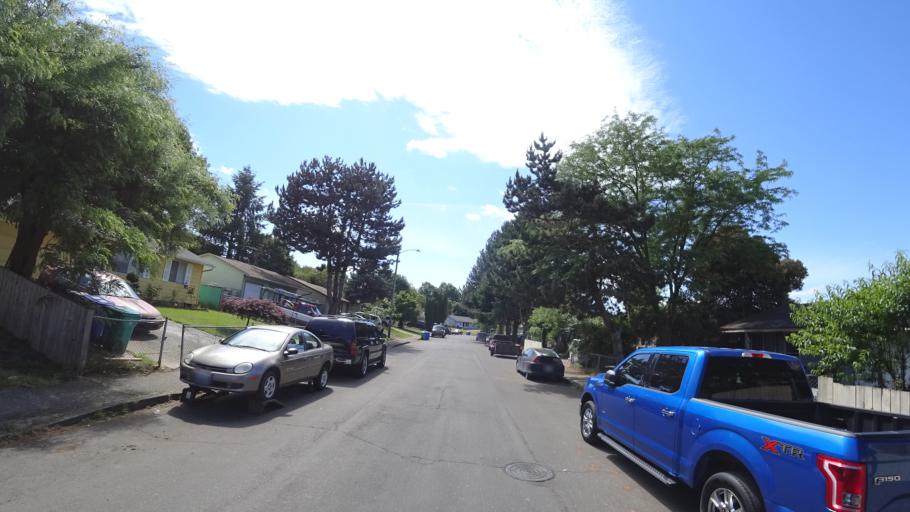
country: US
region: Washington
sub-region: Clark County
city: Vancouver
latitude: 45.5900
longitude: -122.7081
